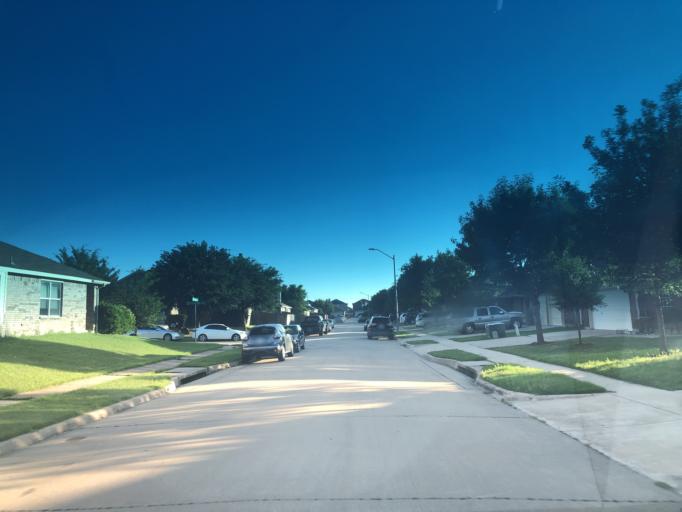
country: US
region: Texas
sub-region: Dallas County
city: Grand Prairie
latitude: 32.7029
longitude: -97.0172
